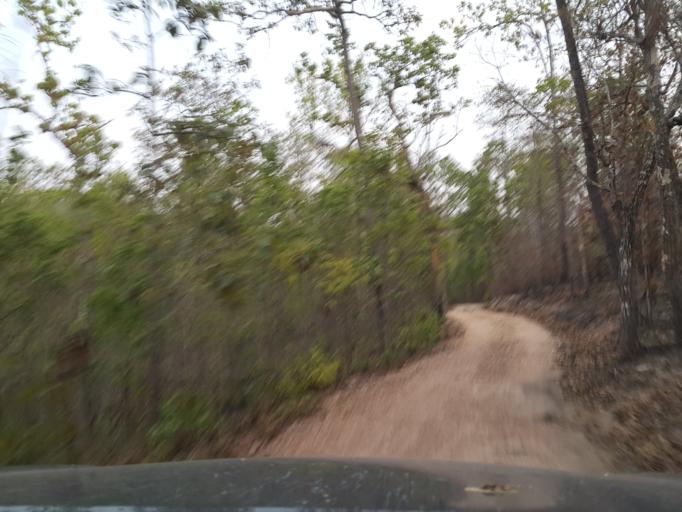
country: TH
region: Lamphun
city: Thung Hua Chang
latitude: 17.9082
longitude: 99.0812
